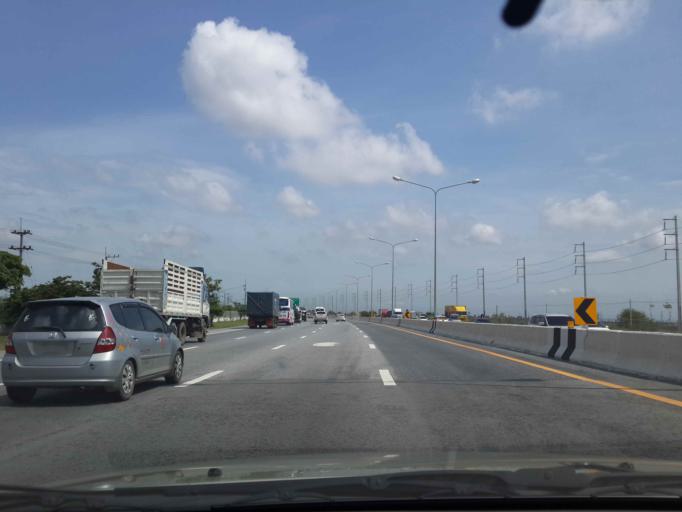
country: TH
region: Chachoengsao
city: Bang Pakong
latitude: 13.5909
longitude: 100.9655
